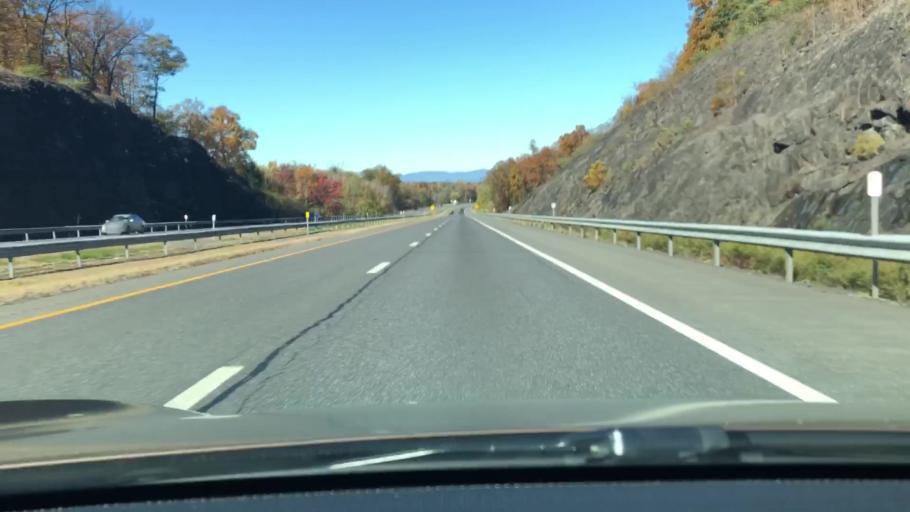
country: US
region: New York
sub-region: Ulster County
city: Tillson
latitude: 41.8108
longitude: -74.0536
